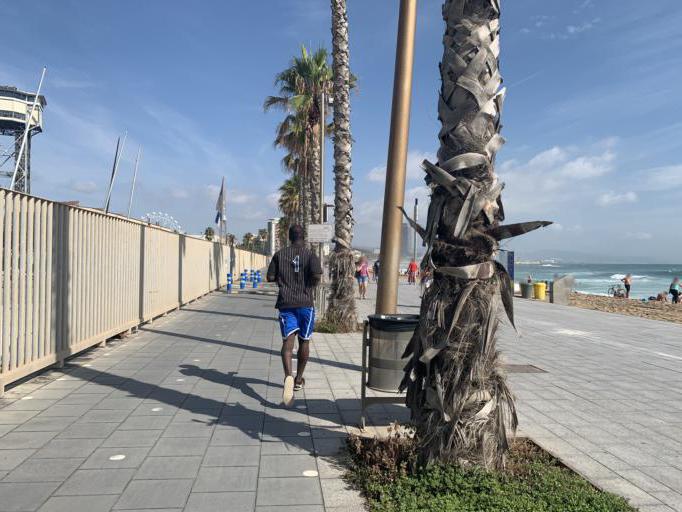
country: ES
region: Catalonia
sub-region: Provincia de Barcelona
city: Ciutat Vella
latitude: 41.3707
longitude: 2.1889
